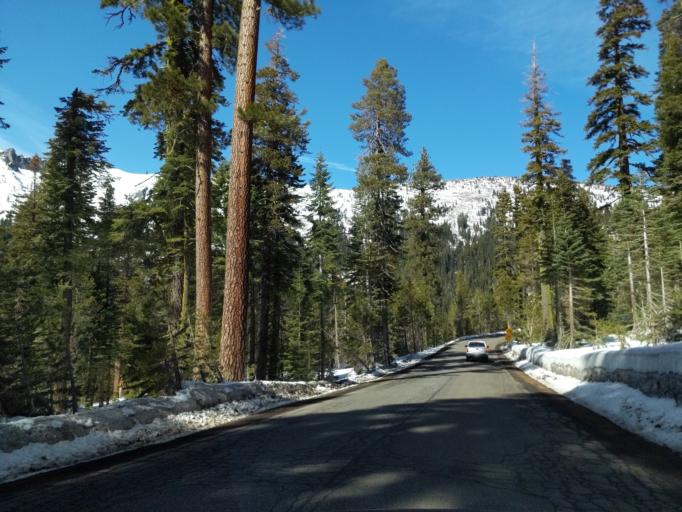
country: US
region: California
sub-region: El Dorado County
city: South Lake Tahoe
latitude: 38.8119
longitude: -120.0810
